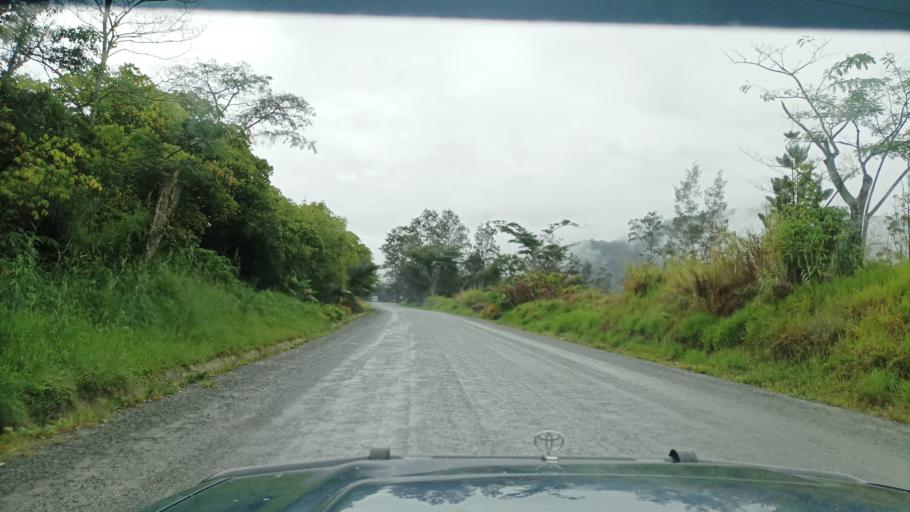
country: PG
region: Western Highlands
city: Rauna
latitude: -5.8332
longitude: 144.3554
